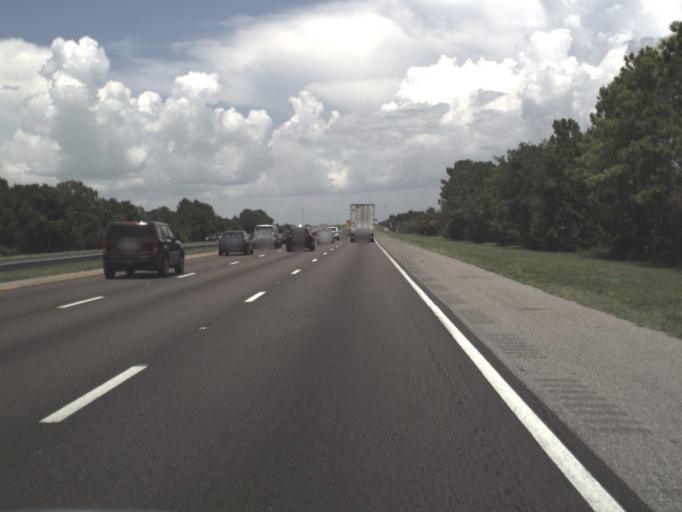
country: US
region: Florida
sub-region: Hillsborough County
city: Gibsonton
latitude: 27.8258
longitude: -82.3513
